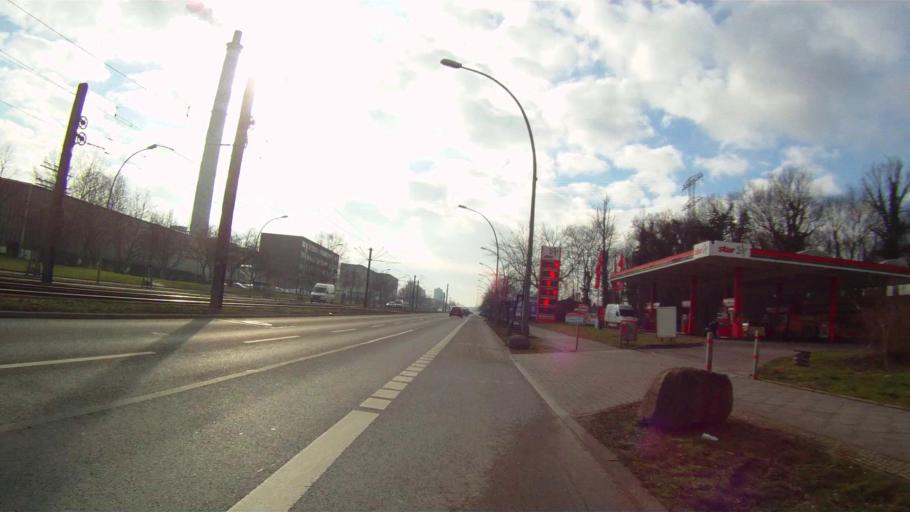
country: DE
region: Berlin
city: Friedrichsfelde
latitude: 52.5231
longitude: 13.5195
